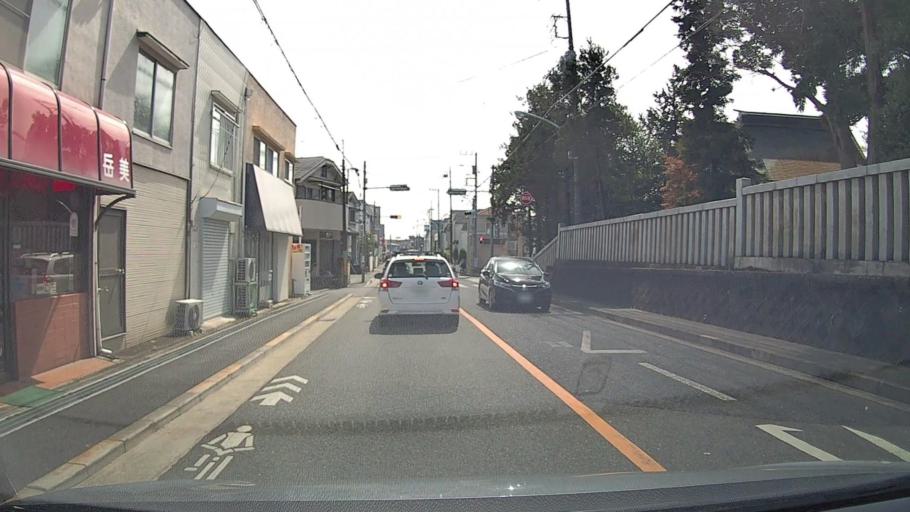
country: JP
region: Tokyo
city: Tanashicho
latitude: 35.7442
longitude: 139.5502
